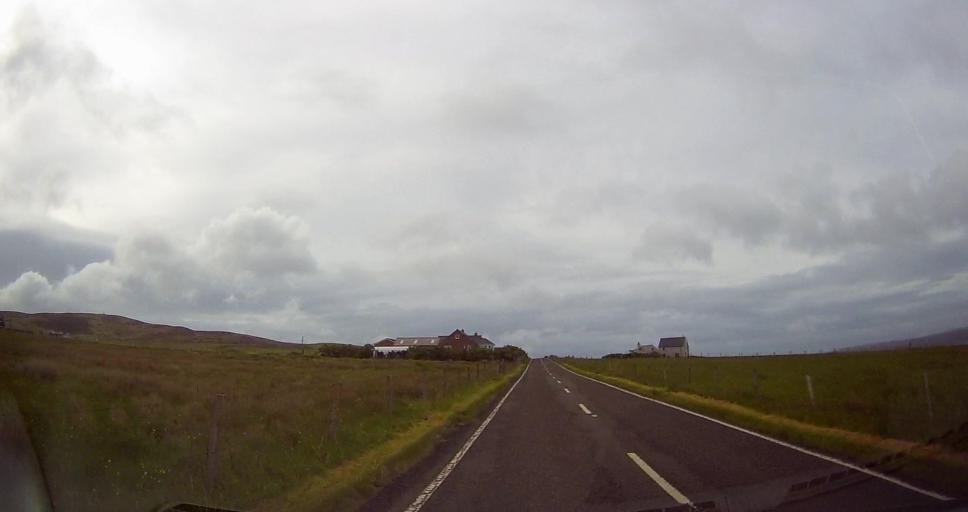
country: GB
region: Scotland
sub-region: Orkney Islands
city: Stromness
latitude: 58.9333
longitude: -3.2093
